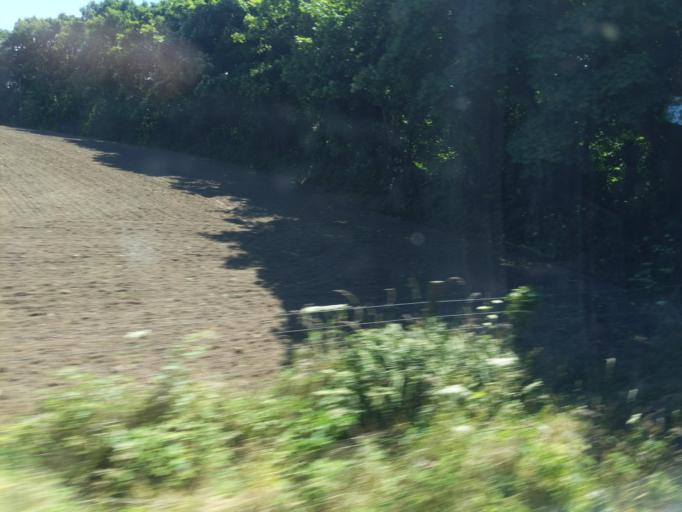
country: GB
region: England
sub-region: Cornwall
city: Saint Stephen
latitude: 50.3351
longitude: -4.8439
